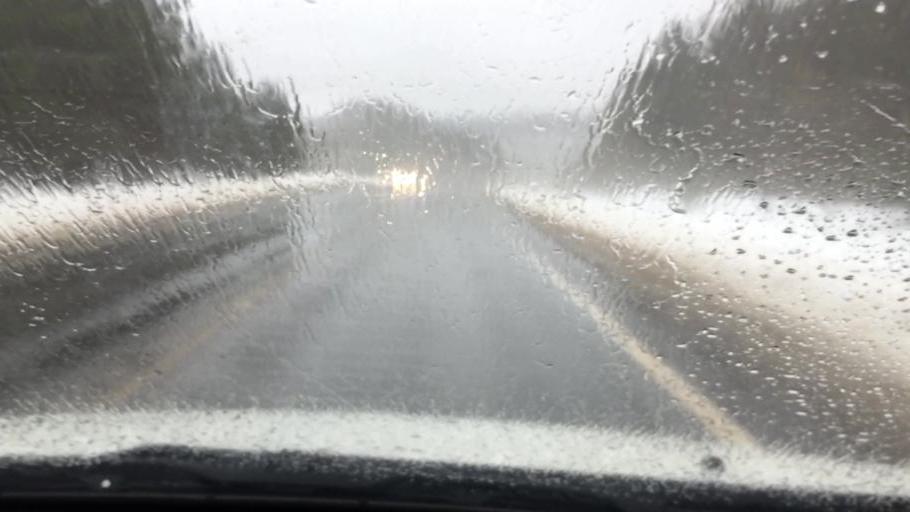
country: US
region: Michigan
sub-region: Antrim County
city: Mancelona
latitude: 44.9604
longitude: -85.0510
